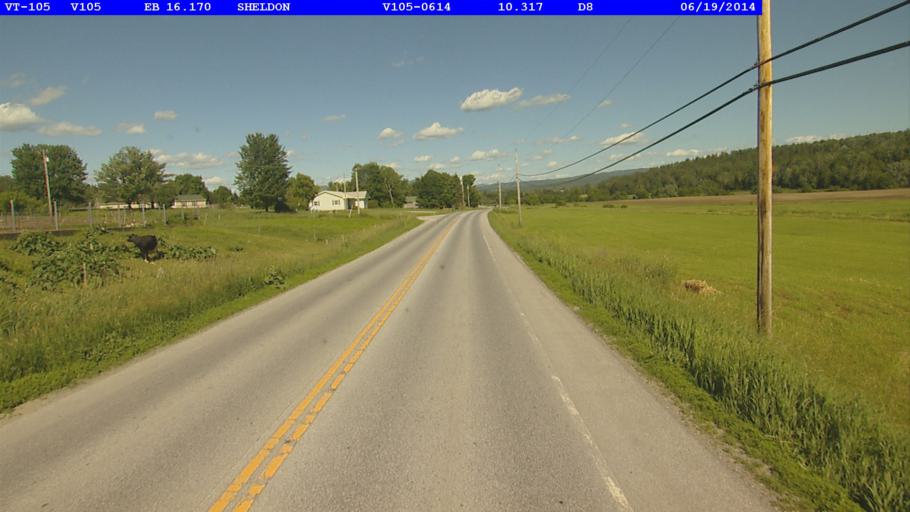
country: US
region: Vermont
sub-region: Franklin County
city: Enosburg Falls
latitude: 44.9073
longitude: -72.8337
